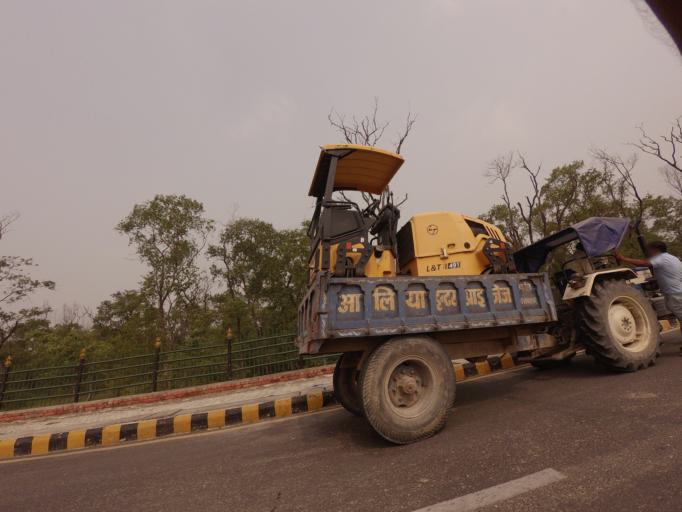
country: IN
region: Uttar Pradesh
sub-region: Maharajganj
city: Nautanwa
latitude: 27.4809
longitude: 83.2840
